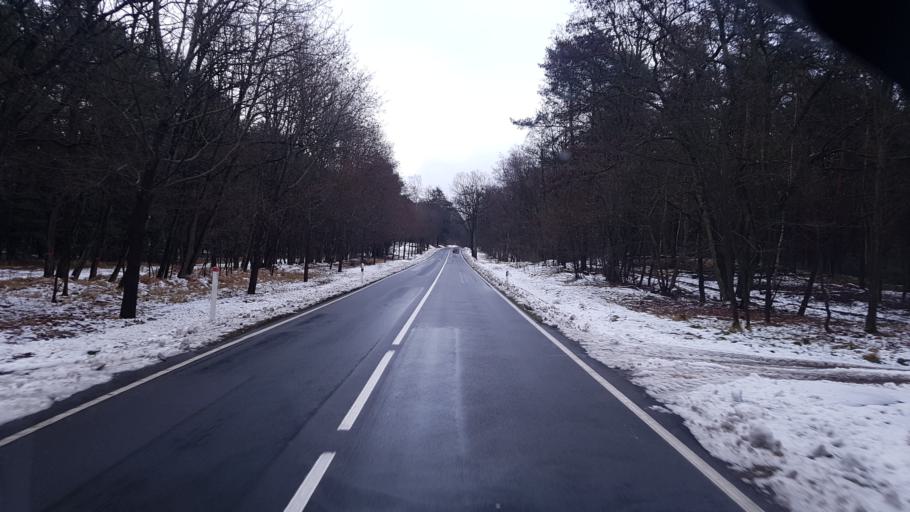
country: DE
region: Brandenburg
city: Jamlitz
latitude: 51.9886
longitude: 14.3802
